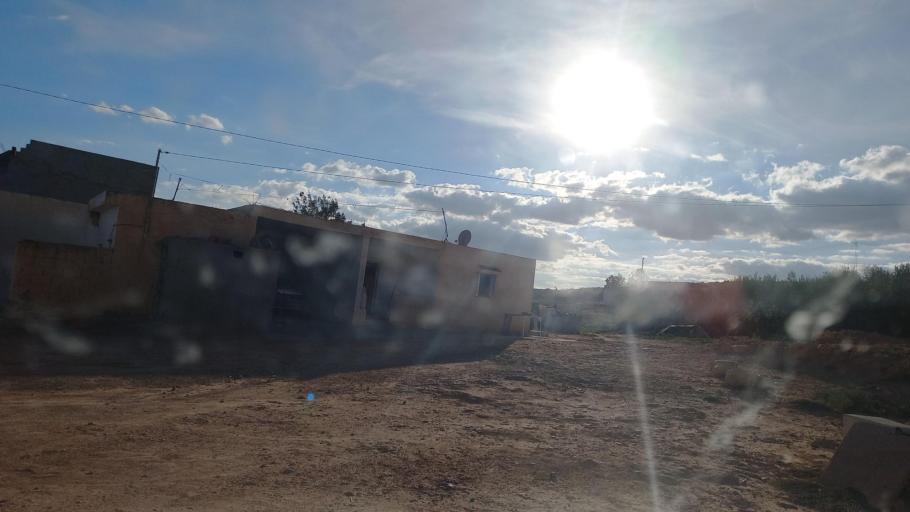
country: TN
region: Al Qasrayn
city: Sbiba
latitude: 35.3816
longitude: 9.0189
